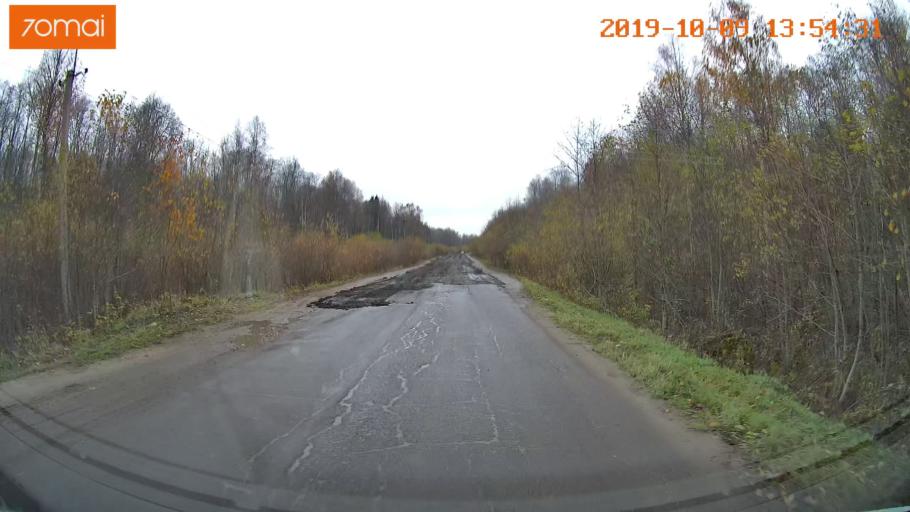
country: RU
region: Kostroma
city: Buy
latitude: 58.4211
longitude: 41.2675
